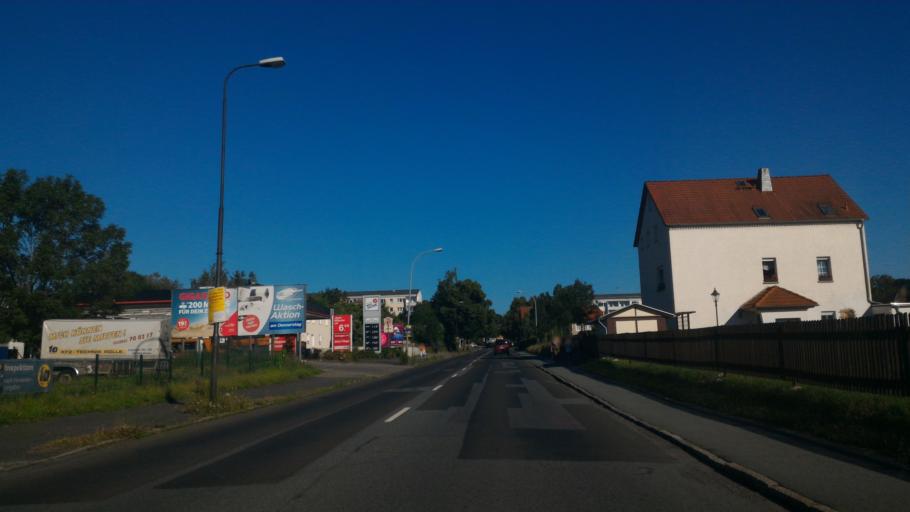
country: DE
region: Saxony
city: Zittau
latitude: 50.9016
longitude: 14.8188
